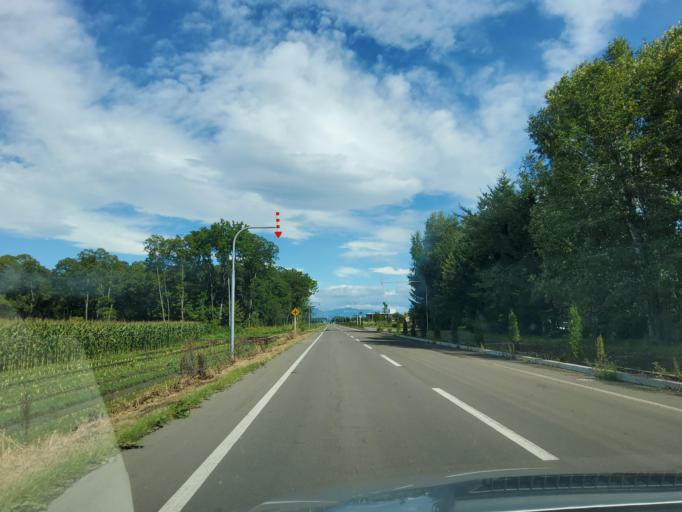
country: JP
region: Hokkaido
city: Otofuke
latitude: 42.9846
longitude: 143.1764
